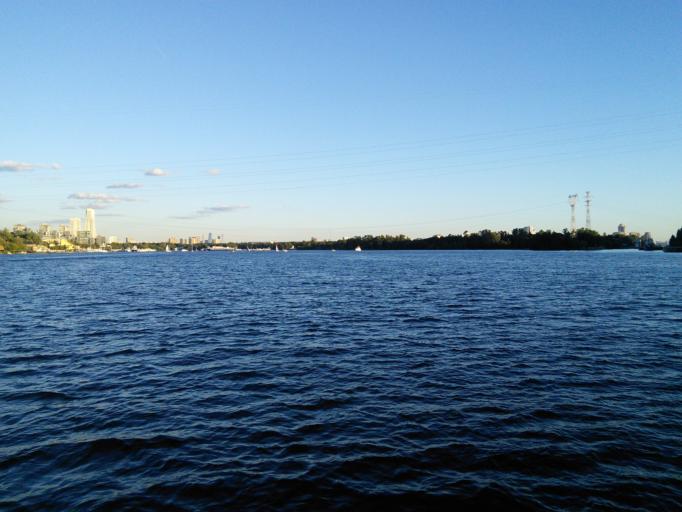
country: RU
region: Moskovskaya
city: Levoberezhnyy
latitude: 55.8435
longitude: 37.4692
